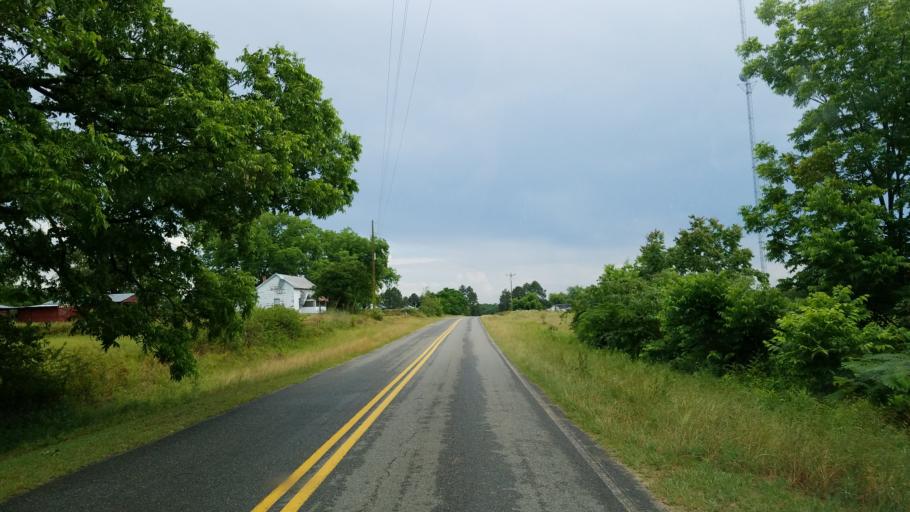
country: US
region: Georgia
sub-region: Dooly County
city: Unadilla
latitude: 32.2431
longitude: -83.7974
